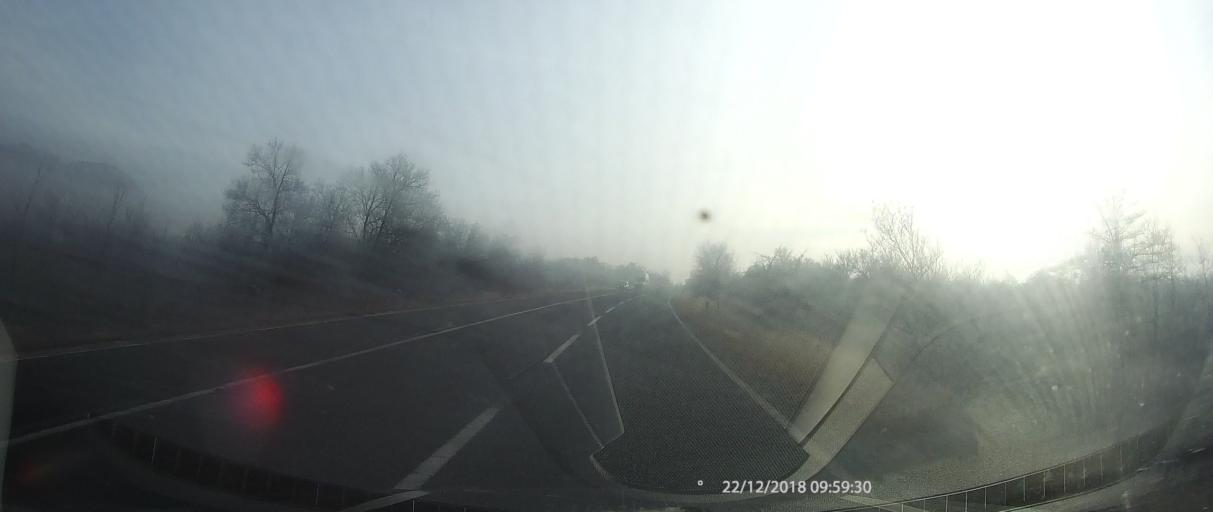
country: MK
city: Klechovce
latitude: 42.1512
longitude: 21.9603
